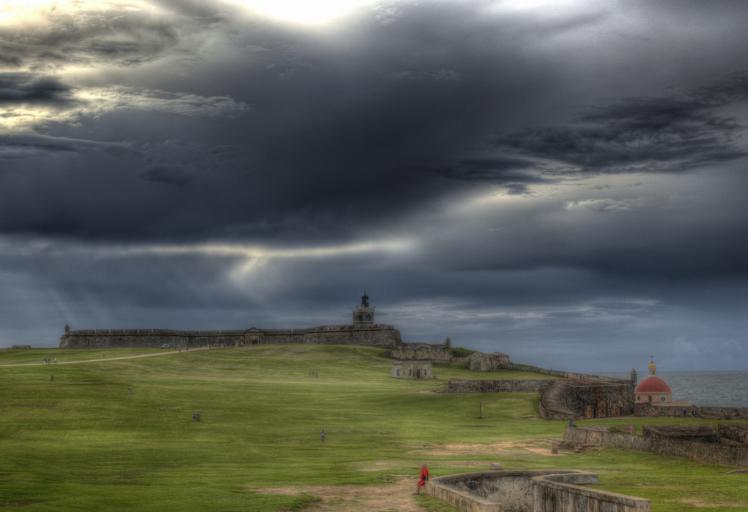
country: PR
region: San Juan
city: San Juan
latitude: 18.4686
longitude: -66.1195
